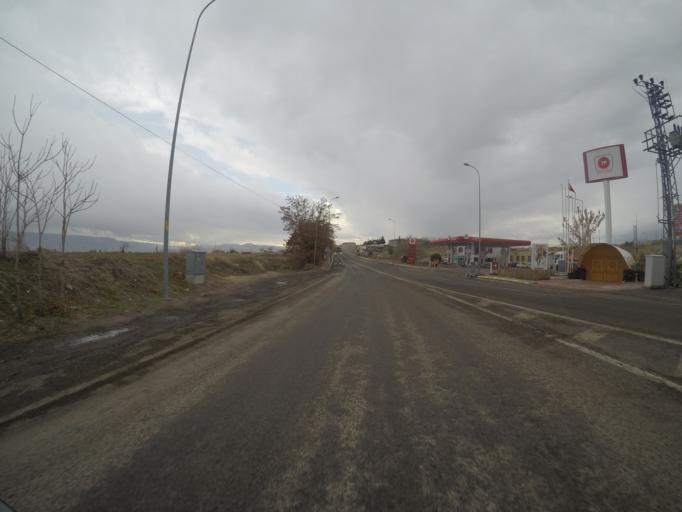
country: TR
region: Nevsehir
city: Goereme
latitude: 38.6337
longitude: 34.8633
